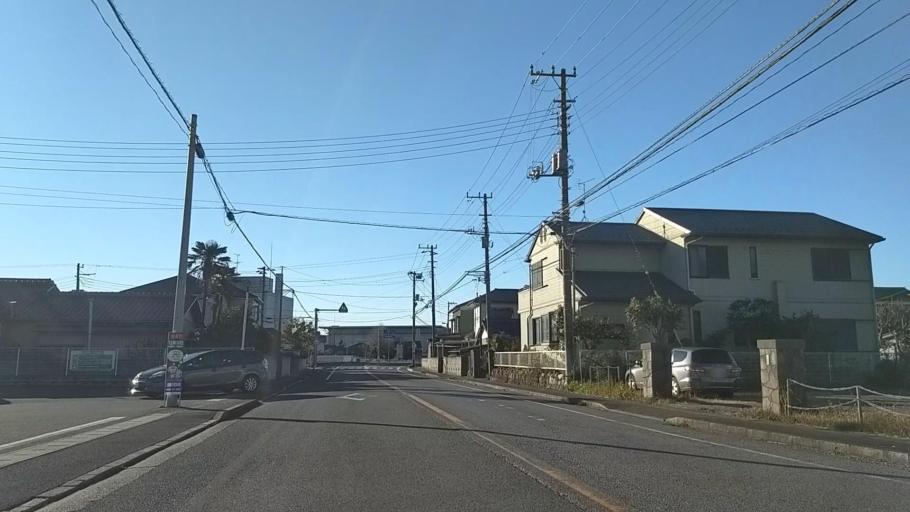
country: JP
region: Chiba
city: Kisarazu
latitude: 35.3775
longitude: 139.9187
